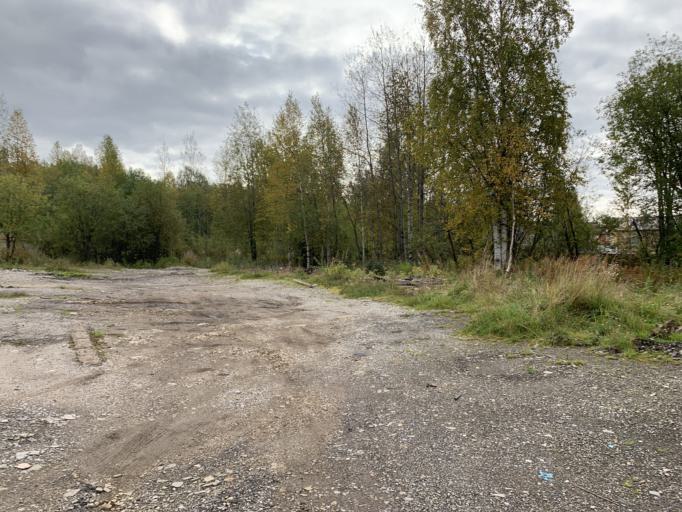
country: RU
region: Perm
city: Gubakha
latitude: 58.8316
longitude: 57.5604
